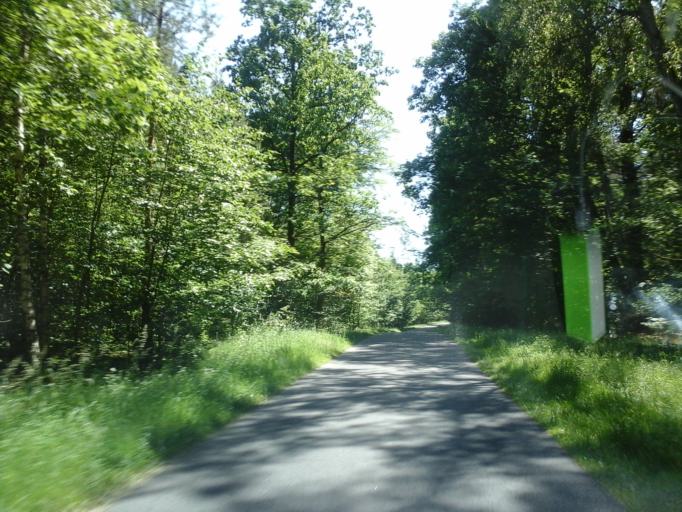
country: PL
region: West Pomeranian Voivodeship
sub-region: Powiat walecki
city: Czlopa
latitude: 53.1021
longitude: 15.9288
